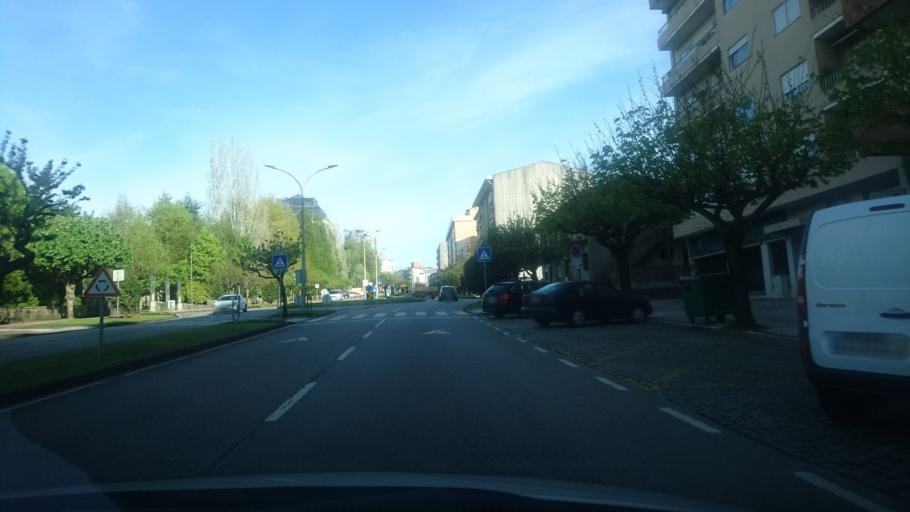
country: PT
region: Aveiro
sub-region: Sao Joao da Madeira
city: Sao Joao da Madeira
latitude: 40.8963
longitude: -8.4862
